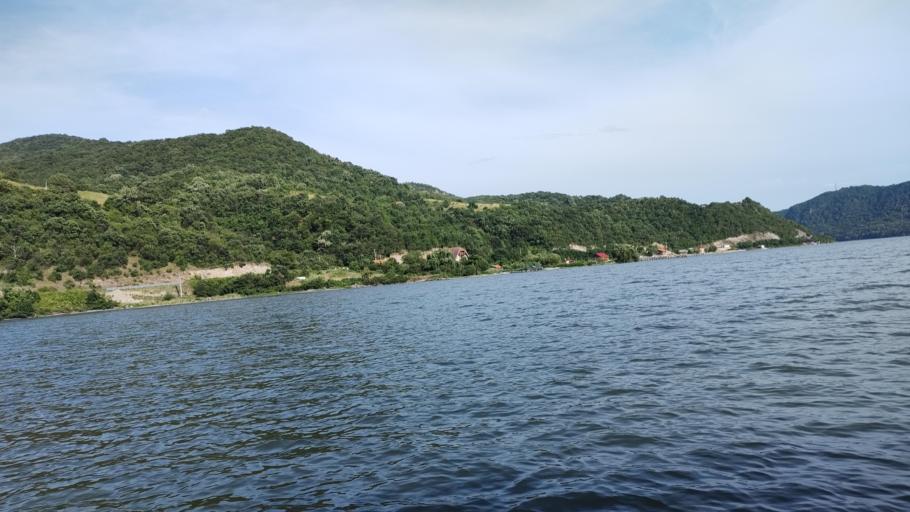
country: RO
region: Mehedinti
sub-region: Comuna Svinita
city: Svinita
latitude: 44.5589
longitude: 22.0317
